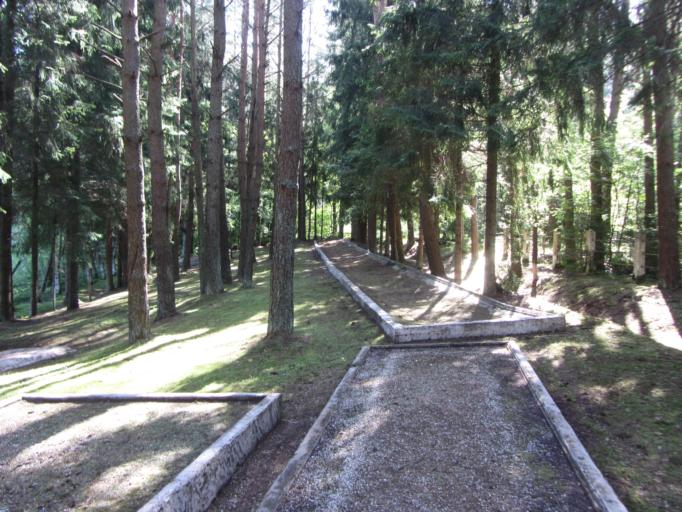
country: LT
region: Utenos apskritis
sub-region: Utena
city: Utena
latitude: 55.5181
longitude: 25.6006
